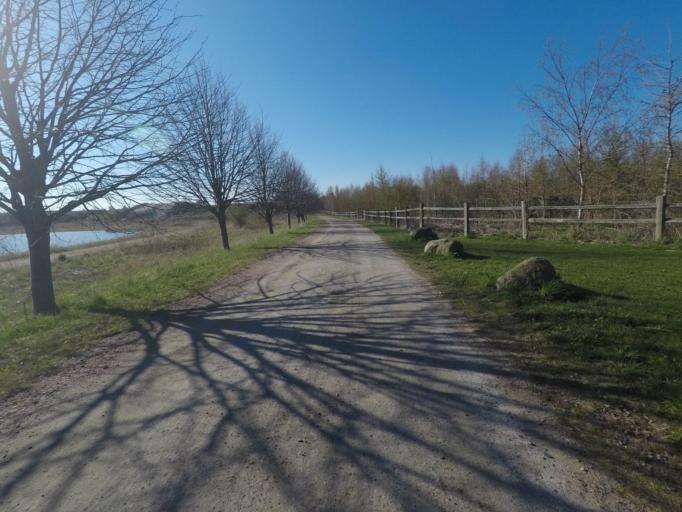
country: SE
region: Skane
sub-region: Malmo
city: Tygelsjo
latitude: 55.5507
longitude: 13.0118
